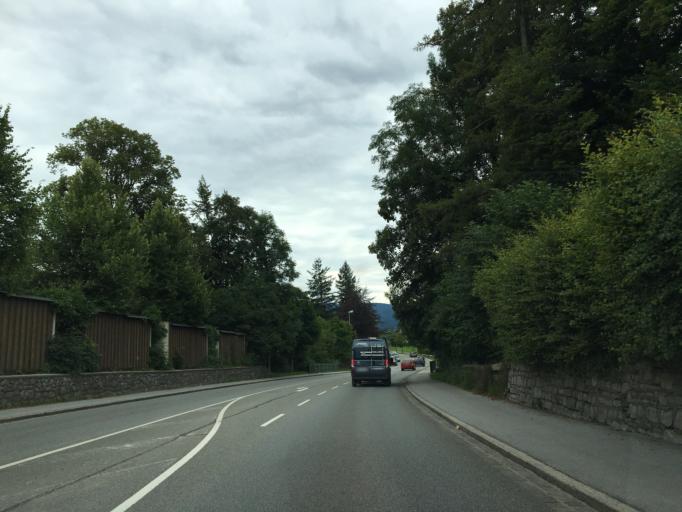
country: DE
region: Bavaria
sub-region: Upper Bavaria
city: Miesbach
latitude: 47.7873
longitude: 11.8381
